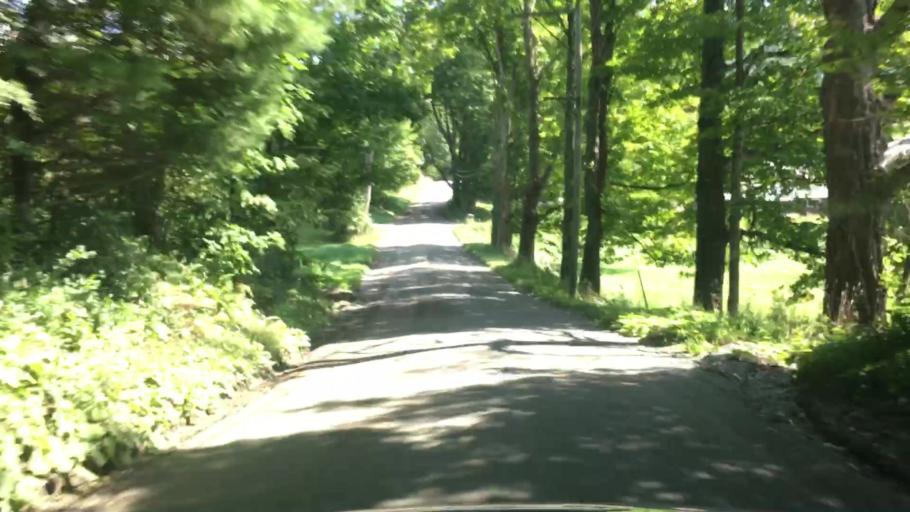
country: US
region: Vermont
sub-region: Windham County
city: West Brattleboro
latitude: 42.7981
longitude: -72.6617
